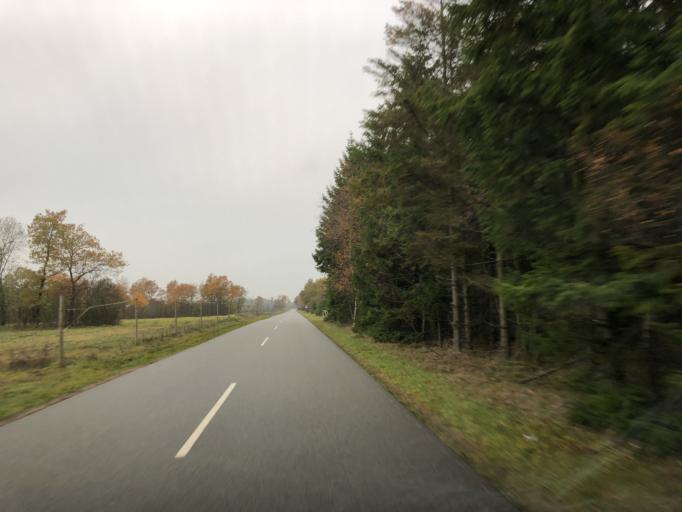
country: DK
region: Central Jutland
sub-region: Herning Kommune
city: Snejbjerg
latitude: 56.2265
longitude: 8.9167
